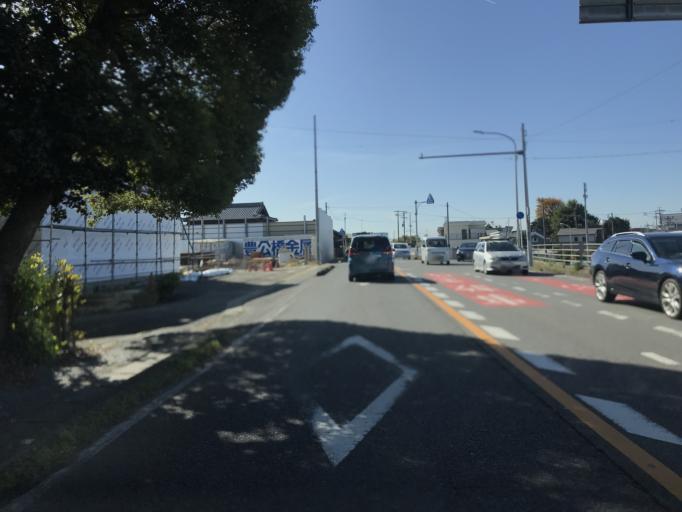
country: JP
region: Aichi
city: Kanie
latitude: 35.1808
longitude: 136.8423
